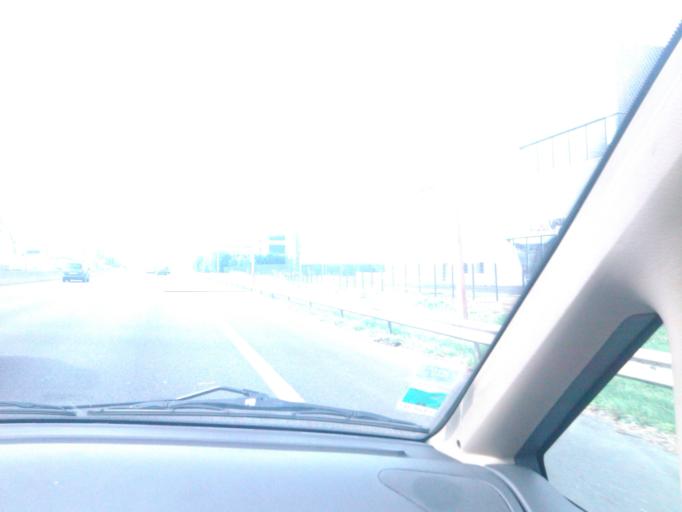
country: FR
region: Ile-de-France
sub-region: Departement des Yvelines
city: Velizy-Villacoublay
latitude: 48.7800
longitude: 2.1872
